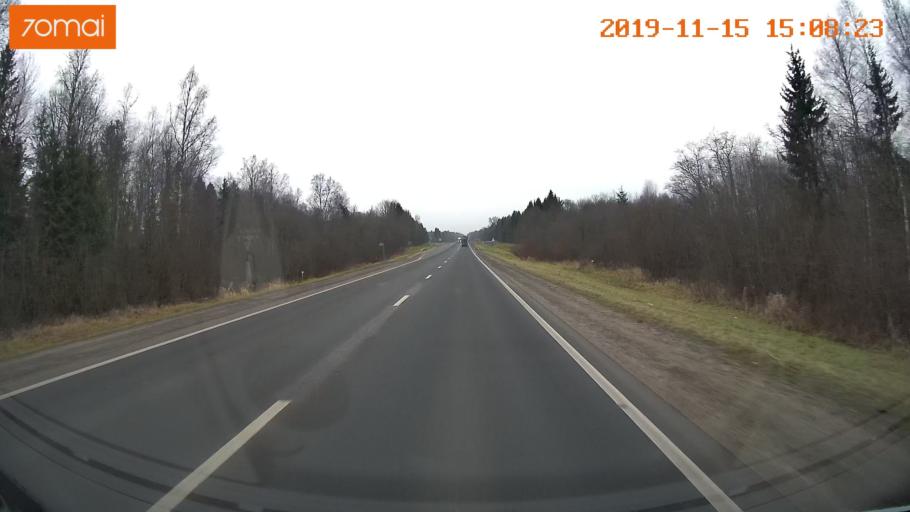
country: RU
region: Jaroslavl
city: Prechistoye
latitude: 58.3716
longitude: 40.2775
